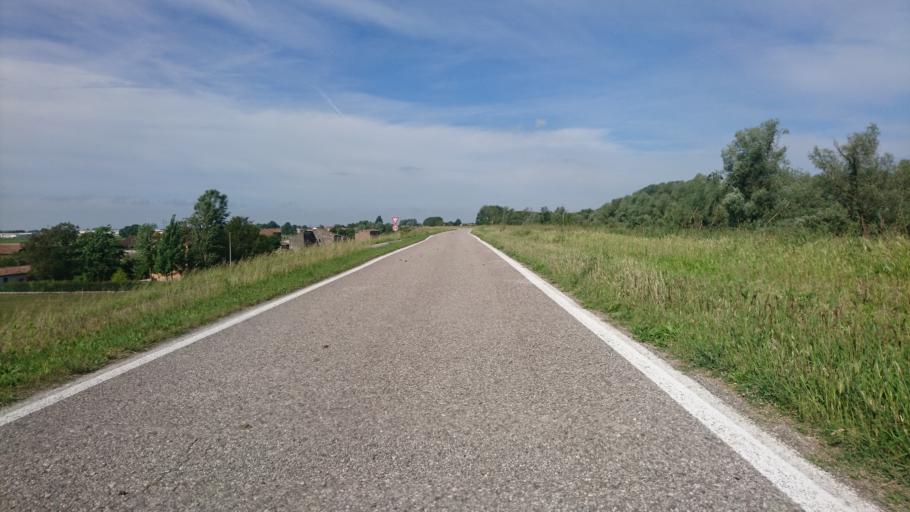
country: IT
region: Lombardy
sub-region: Provincia di Mantova
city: Carbonara di Po
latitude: 45.0386
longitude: 11.2452
